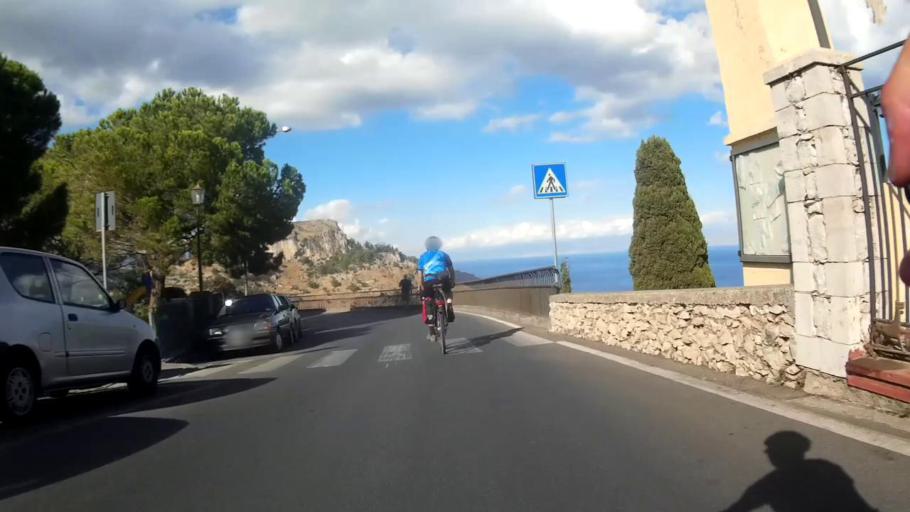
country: IT
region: Sicily
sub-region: Messina
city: Castelmola
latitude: 37.8597
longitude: 15.2775
